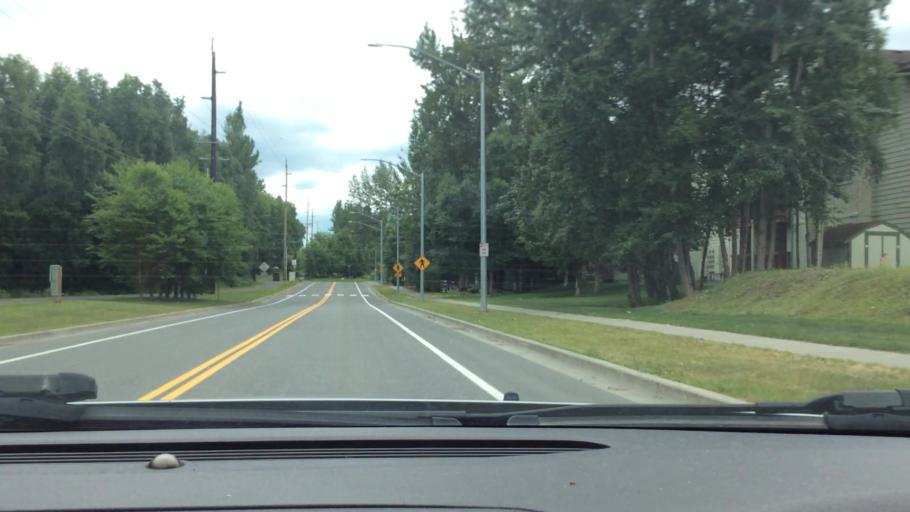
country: US
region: Alaska
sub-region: Anchorage Municipality
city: Anchorage
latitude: 61.2060
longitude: -149.7934
